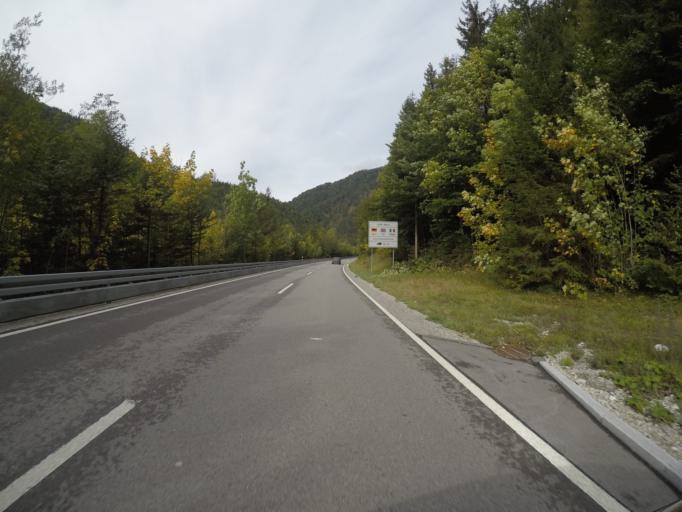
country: AT
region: Tyrol
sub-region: Politischer Bezirk Schwaz
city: Achenkirch
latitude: 47.5812
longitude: 11.6303
